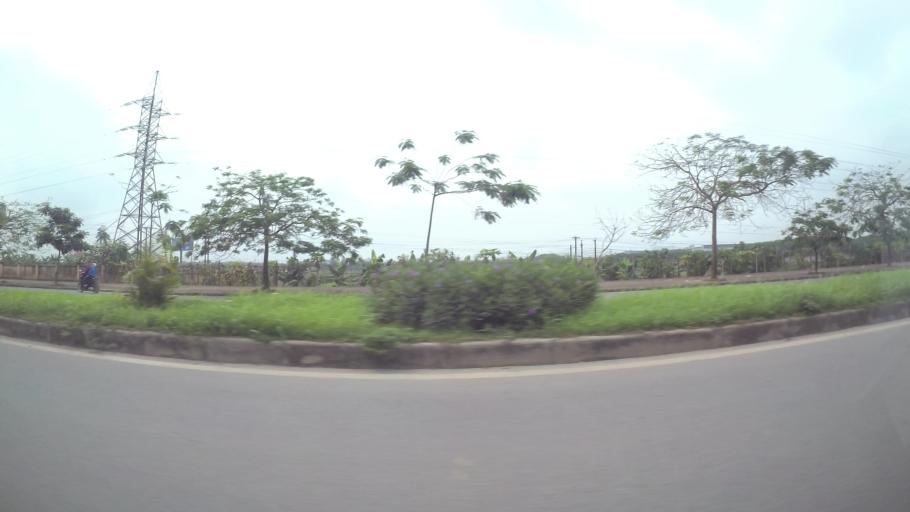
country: VN
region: Ha Noi
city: Trau Quy
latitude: 21.0319
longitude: 105.9297
